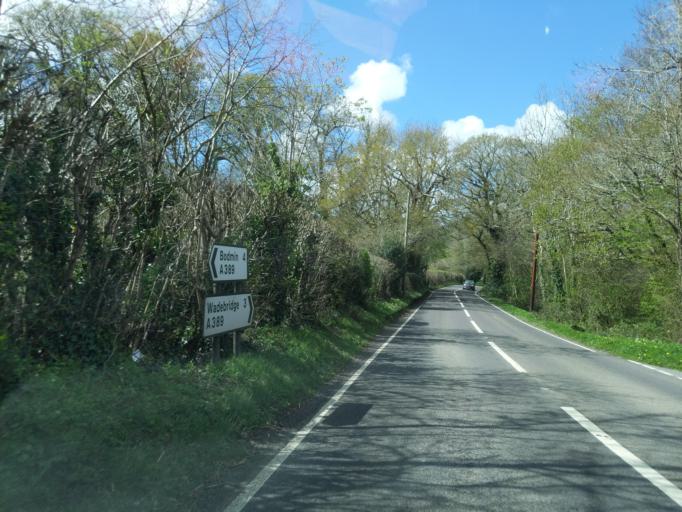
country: GB
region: England
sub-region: Cornwall
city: Wadebridge
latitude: 50.5045
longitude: -4.7790
